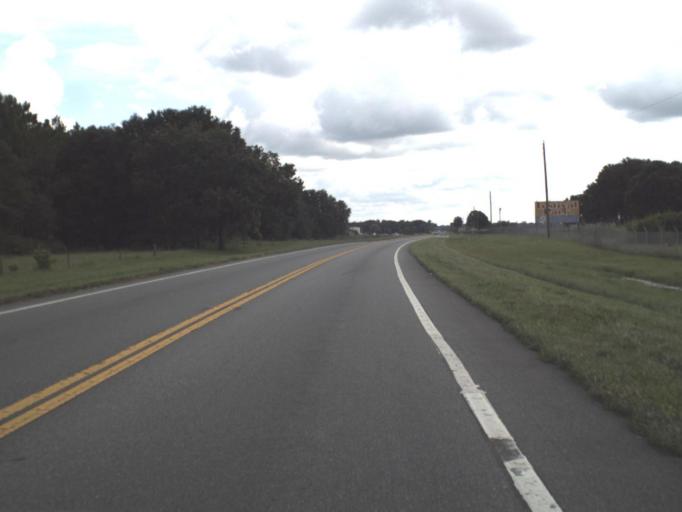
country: US
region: Florida
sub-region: Pasco County
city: Zephyrhills South
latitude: 28.1901
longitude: -82.2036
